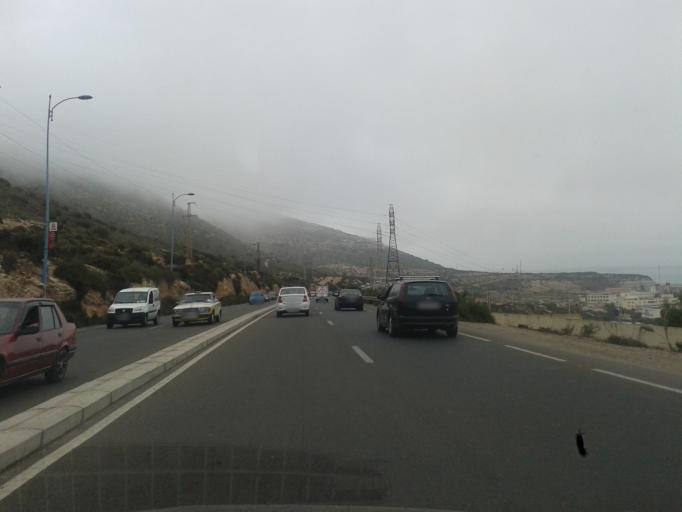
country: MA
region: Souss-Massa-Draa
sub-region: Agadir-Ida-ou-Tnan
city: Agadir
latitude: 30.4343
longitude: -9.6390
